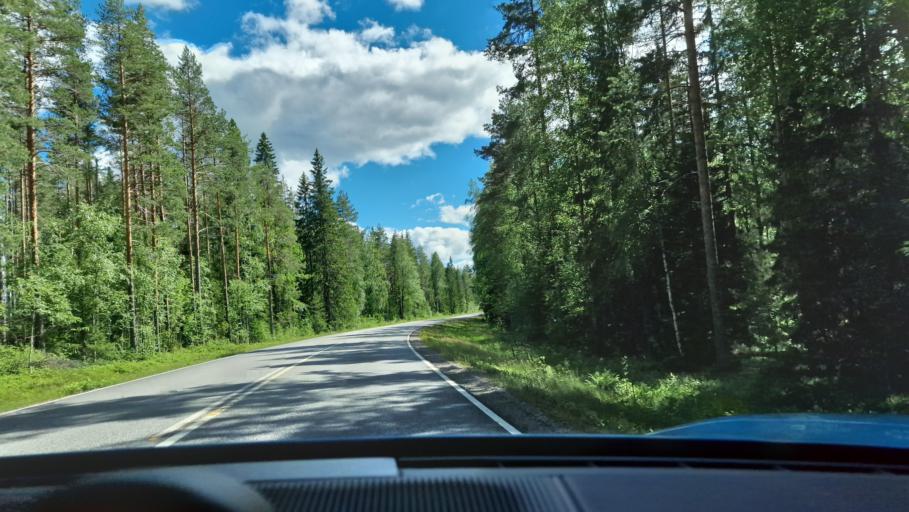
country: FI
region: Central Finland
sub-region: Saarijaervi-Viitasaari
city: Pylkoenmaeki
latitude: 62.6454
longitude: 24.5746
